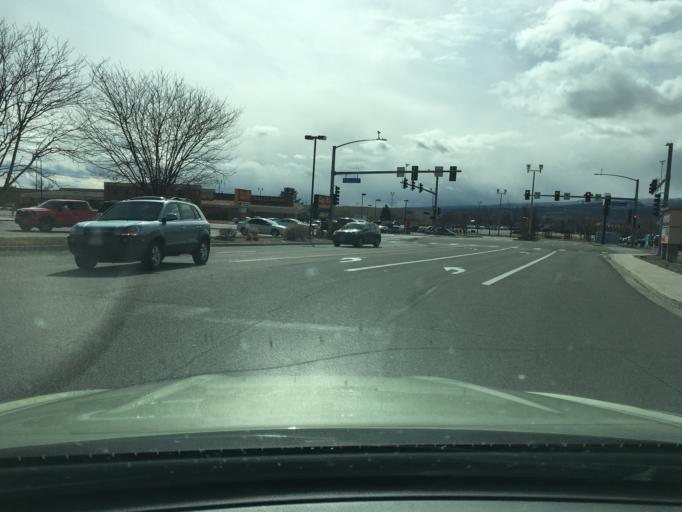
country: US
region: Colorado
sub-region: Mesa County
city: Redlands
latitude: 39.0953
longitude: -108.6059
